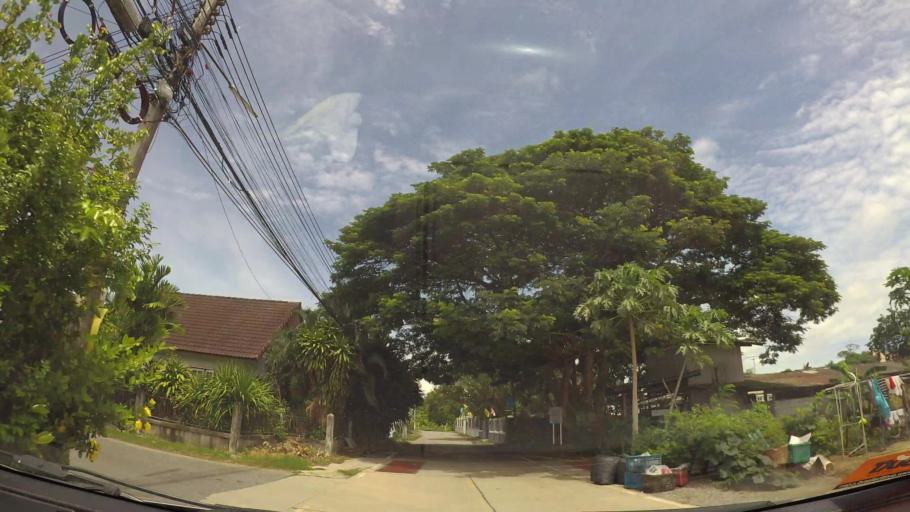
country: TH
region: Chon Buri
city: Sattahip
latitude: 12.7031
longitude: 100.8849
